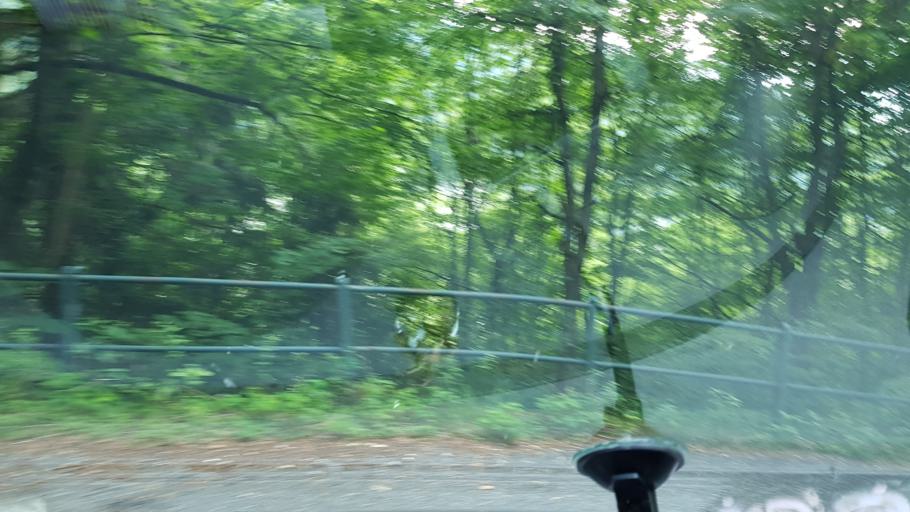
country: IT
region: Friuli Venezia Giulia
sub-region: Provincia di Udine
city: Prato
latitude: 46.3457
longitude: 13.3976
